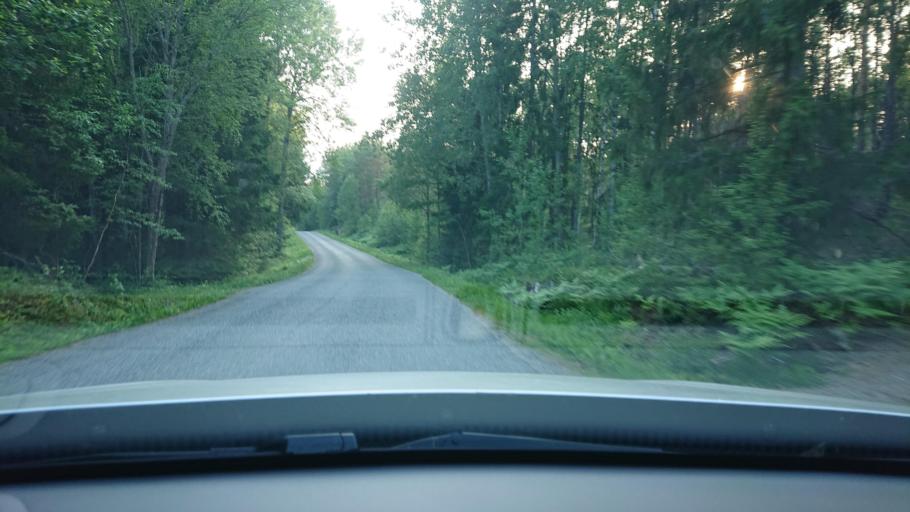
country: SE
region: Stockholm
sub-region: Osterakers Kommun
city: Akersberga
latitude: 59.5201
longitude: 18.3323
